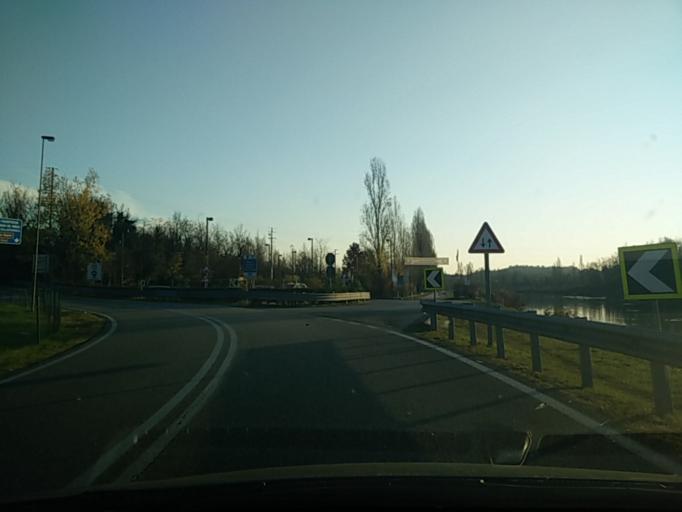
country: IT
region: Veneto
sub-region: Provincia di Verona
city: Peschiera del Garda
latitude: 45.4283
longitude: 10.7013
